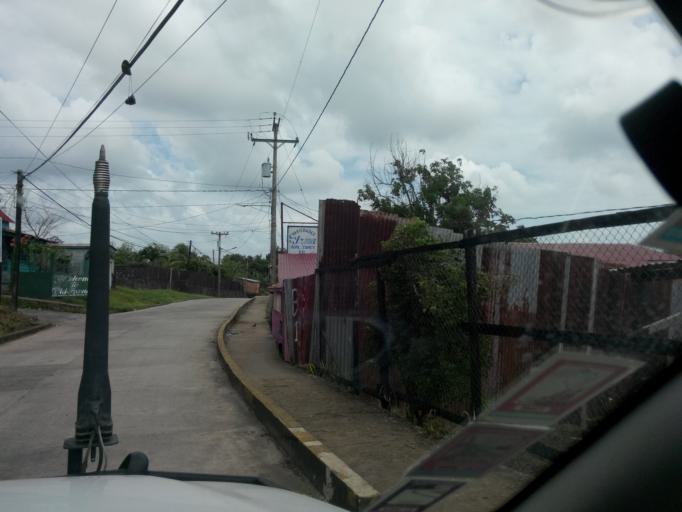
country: NI
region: Atlantico Sur
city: Bluefields
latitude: 12.0179
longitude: -83.7624
